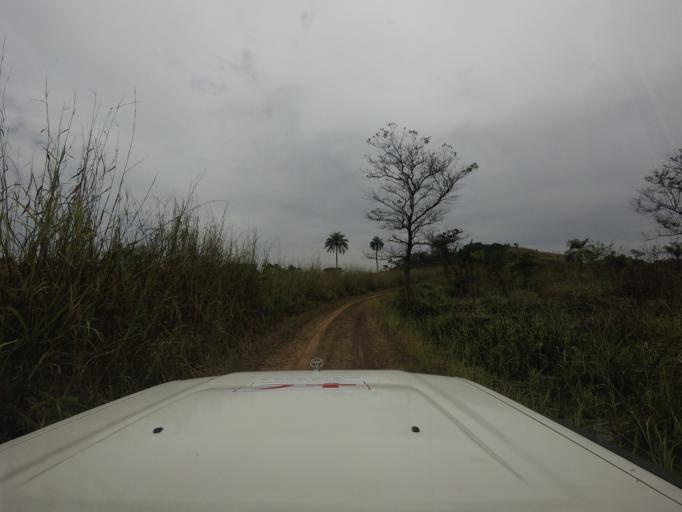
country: SL
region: Eastern Province
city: Buedu
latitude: 8.2518
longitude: -10.2902
